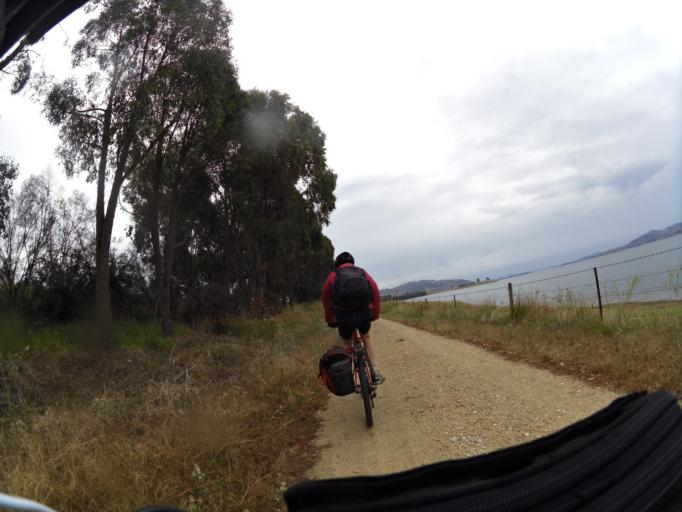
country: AU
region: New South Wales
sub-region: Albury Municipality
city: East Albury
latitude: -36.2221
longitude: 147.0721
